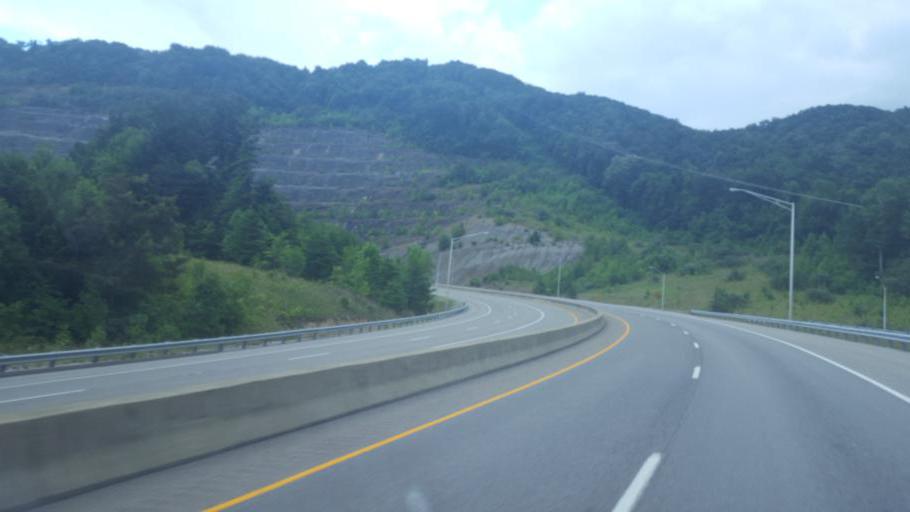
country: US
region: Kentucky
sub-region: Letcher County
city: Jenkins
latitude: 37.1593
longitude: -82.6491
